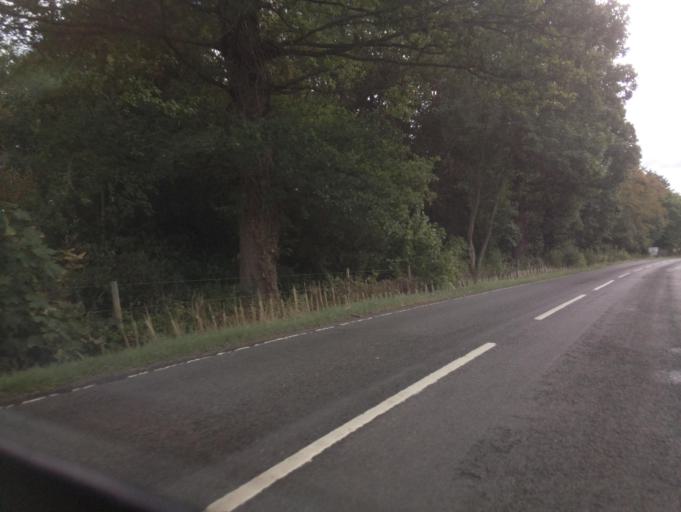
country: GB
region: England
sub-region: Nottinghamshire
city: East Leake
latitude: 52.8107
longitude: -1.1850
